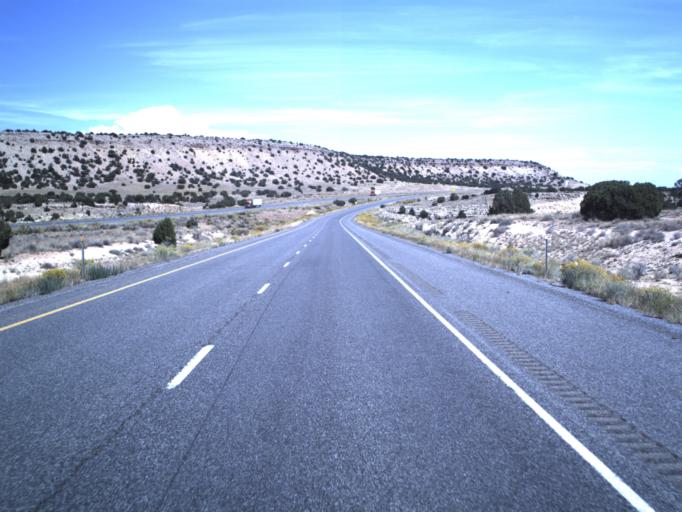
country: US
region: Utah
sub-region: Emery County
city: Castle Dale
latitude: 38.9032
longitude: -110.5600
